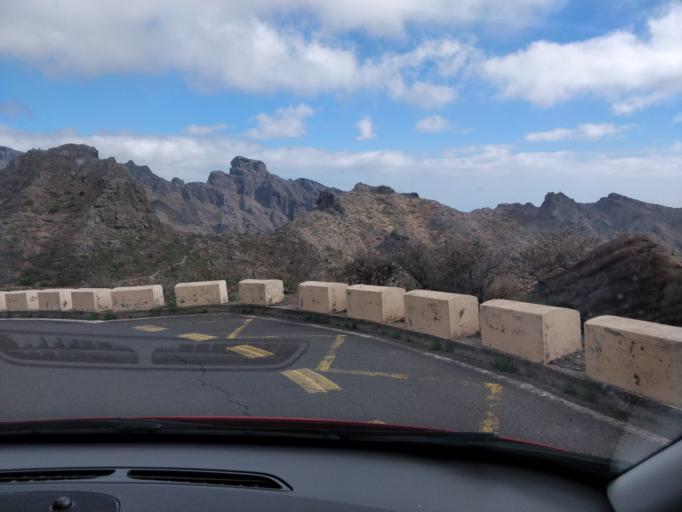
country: ES
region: Canary Islands
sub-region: Provincia de Santa Cruz de Tenerife
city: Tanque
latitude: 28.3227
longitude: -16.8573
